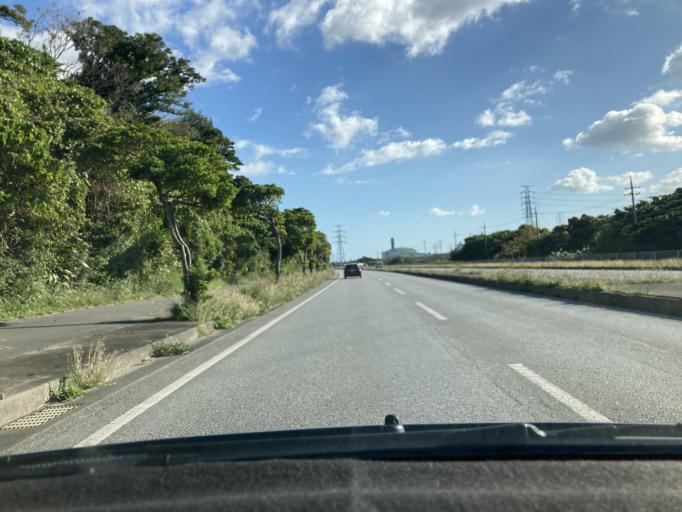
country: JP
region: Okinawa
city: Ishikawa
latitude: 26.4081
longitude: 127.8206
